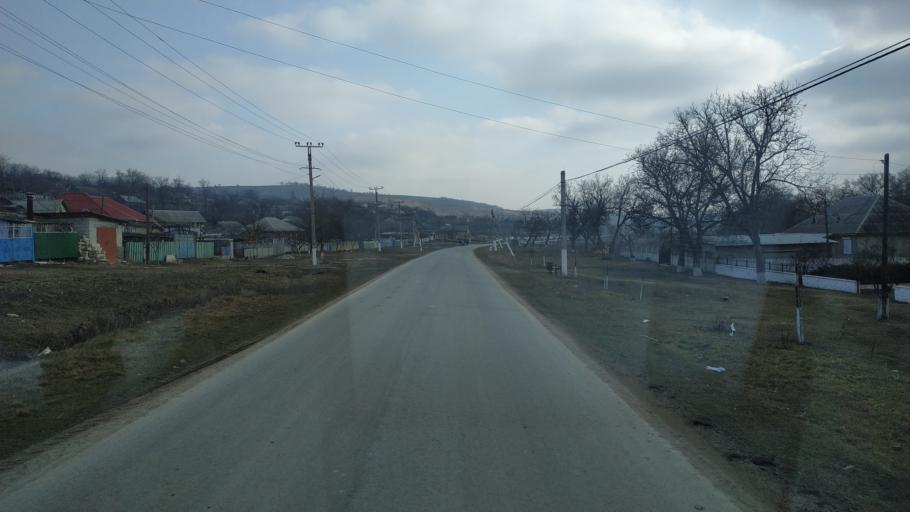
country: MD
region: Nisporeni
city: Nisporeni
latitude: 46.9401
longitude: 28.3265
